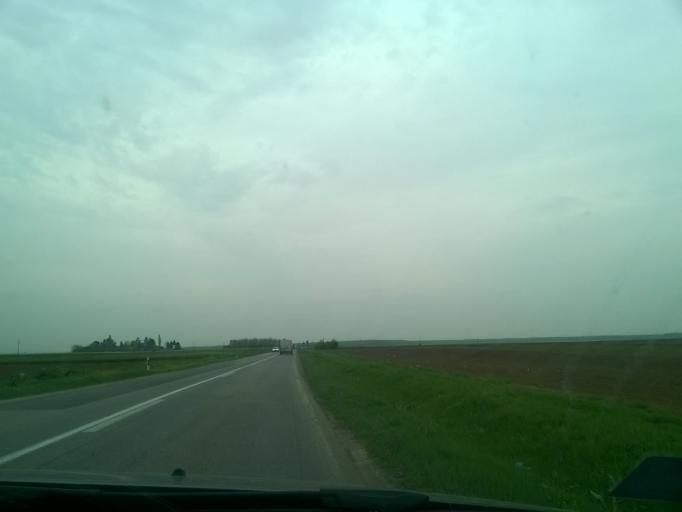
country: RS
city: Hrtkovci
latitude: 44.8620
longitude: 19.7718
